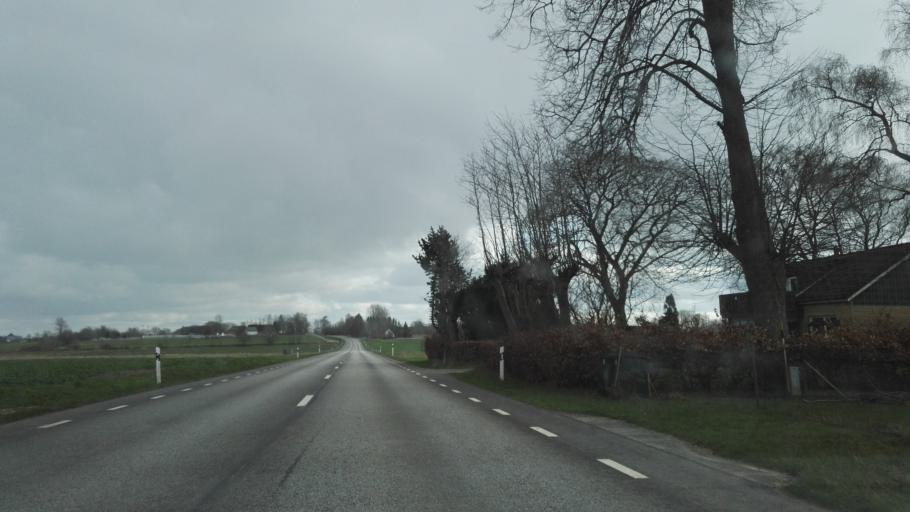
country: SE
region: Skane
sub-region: Horby Kommun
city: Hoerby
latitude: 55.7722
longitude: 13.6740
